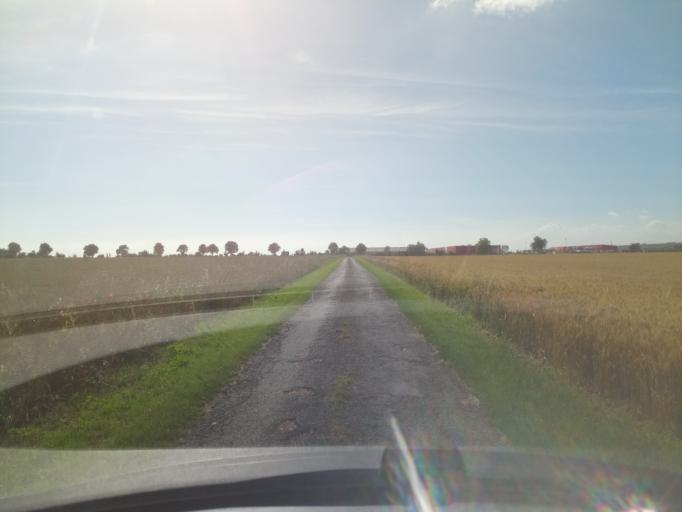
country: FR
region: Poitou-Charentes
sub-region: Departement de la Charente-Maritime
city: Andilly
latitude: 46.2577
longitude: -1.0066
